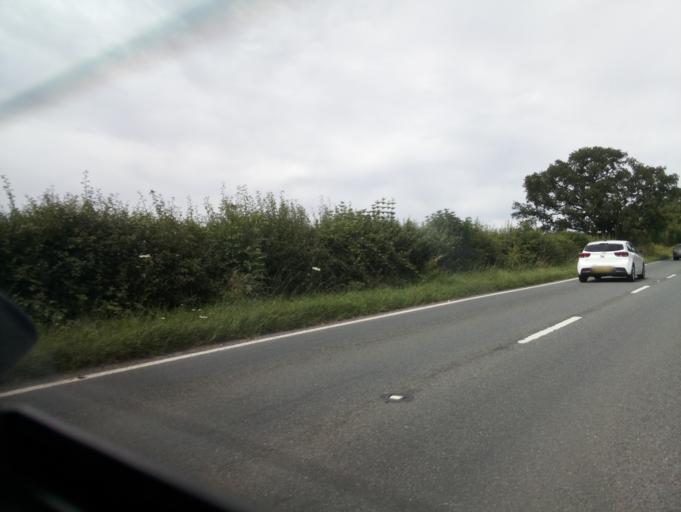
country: GB
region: England
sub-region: Somerset
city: Glastonbury
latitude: 51.1726
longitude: -2.6953
